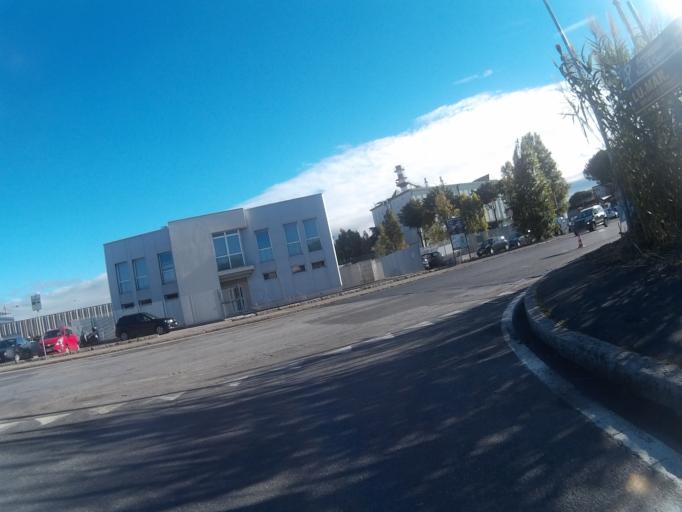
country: IT
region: Tuscany
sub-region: Provincia di Livorno
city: Livorno
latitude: 43.5682
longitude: 10.3405
